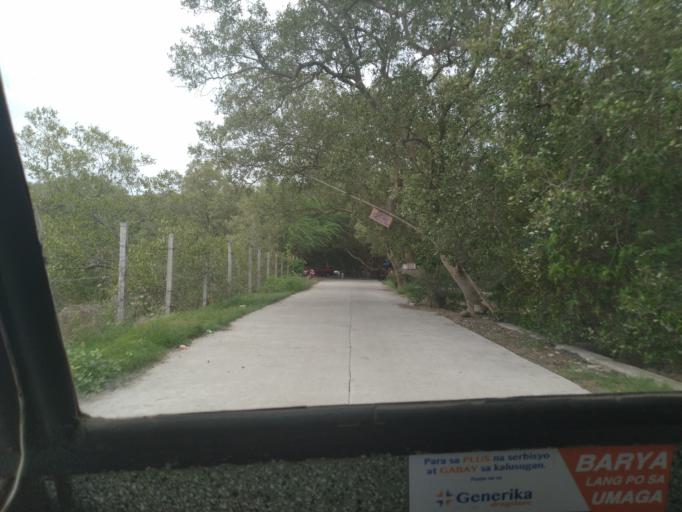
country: PH
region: Central Visayas
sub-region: Province of Negros Oriental
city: Okiot
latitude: 9.5464
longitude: 123.1535
